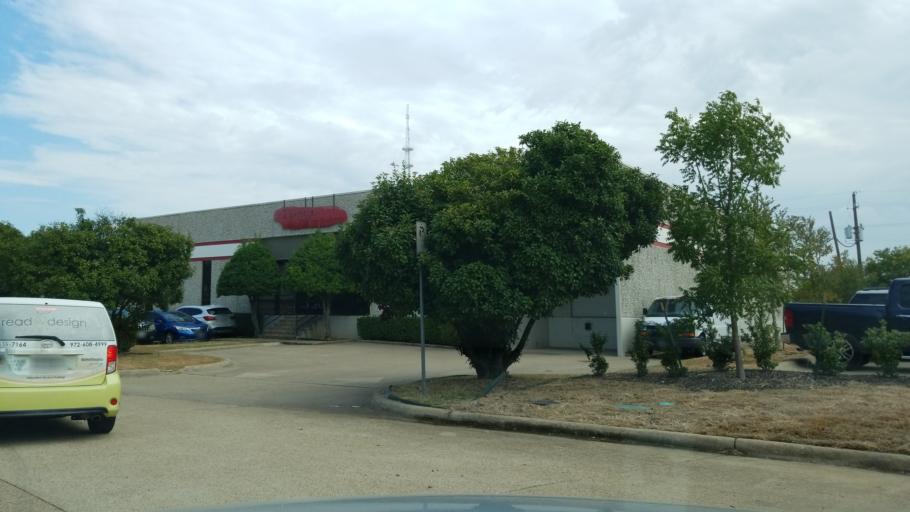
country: US
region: Texas
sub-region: Dallas County
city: Garland
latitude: 32.8977
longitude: -96.6926
